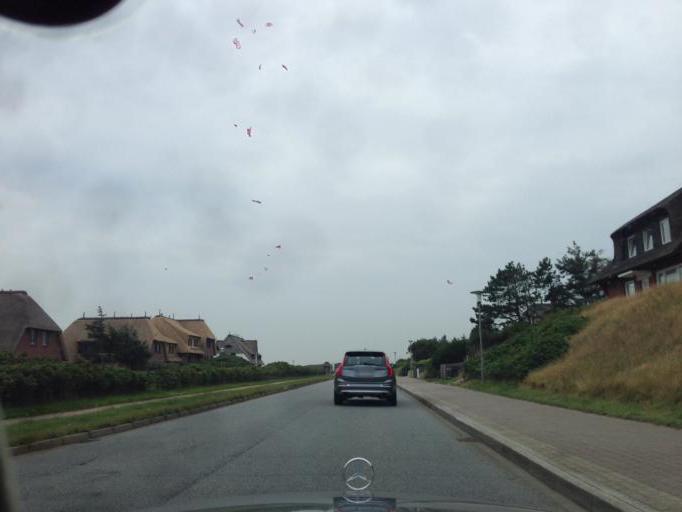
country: DE
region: Schleswig-Holstein
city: Westerland
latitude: 54.8430
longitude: 8.2926
